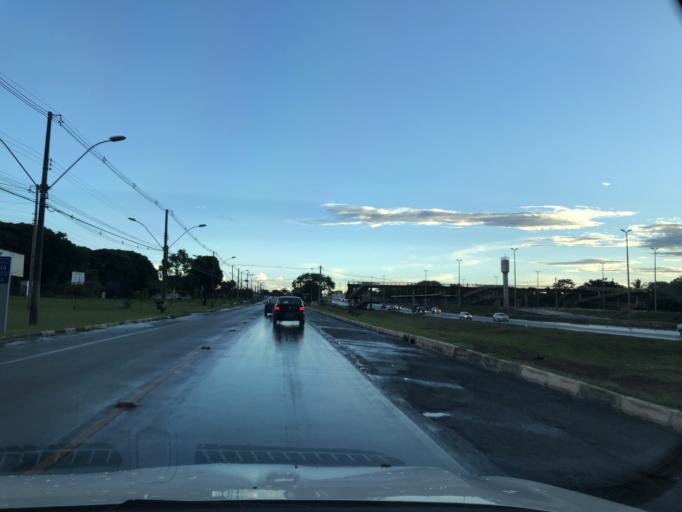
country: BR
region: Federal District
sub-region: Brasilia
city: Brasilia
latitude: -15.8778
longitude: -47.9588
